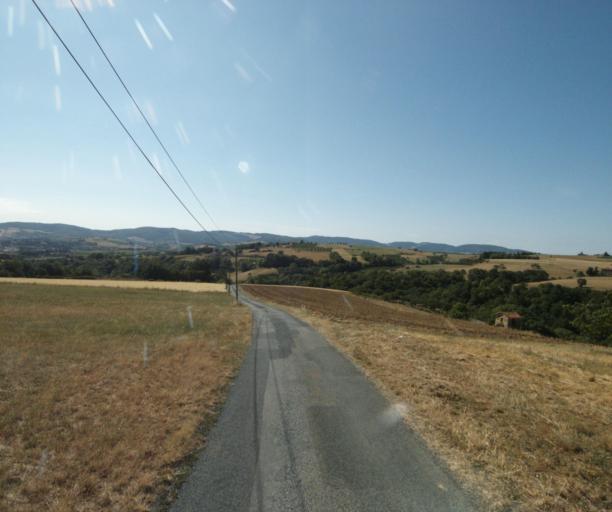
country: FR
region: Rhone-Alpes
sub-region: Departement du Rhone
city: Savigny
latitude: 45.8168
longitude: 4.5625
